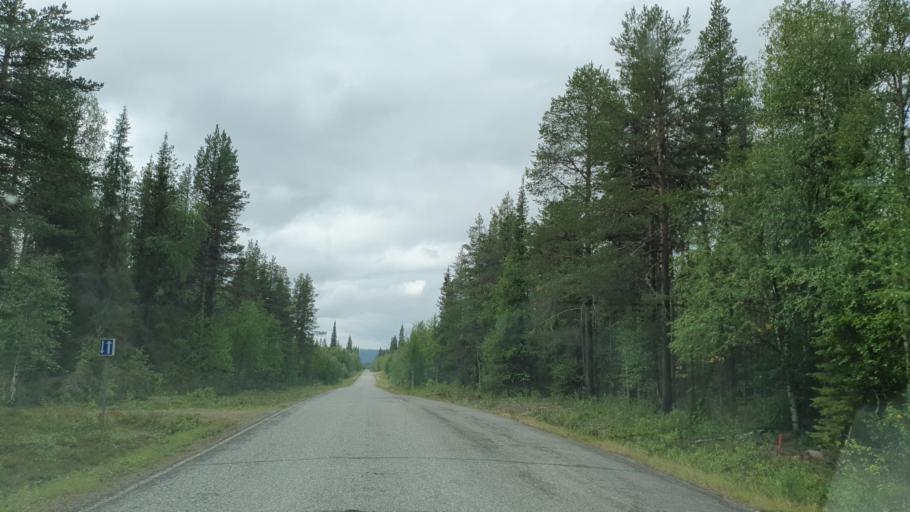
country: FI
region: Lapland
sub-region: Tunturi-Lappi
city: Kittilae
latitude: 67.7374
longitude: 24.3498
